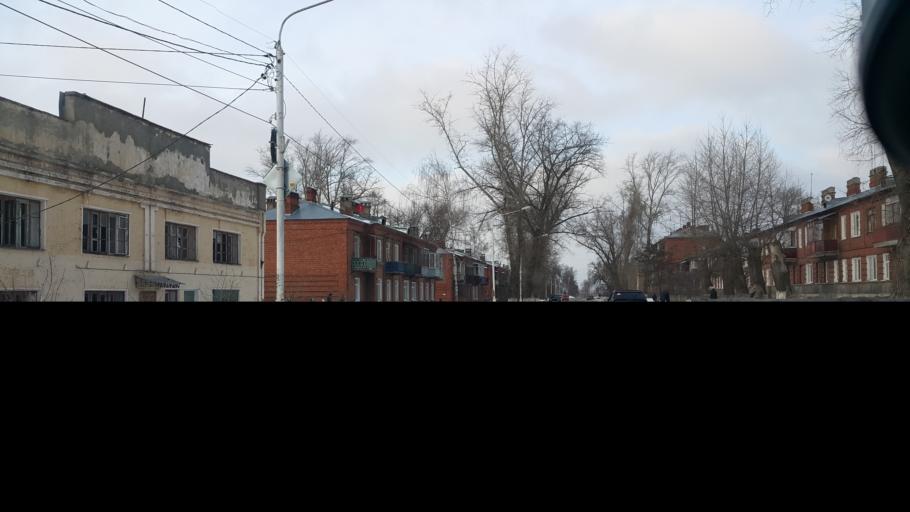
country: RU
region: Tambov
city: Kotovsk
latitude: 52.5960
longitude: 41.4953
